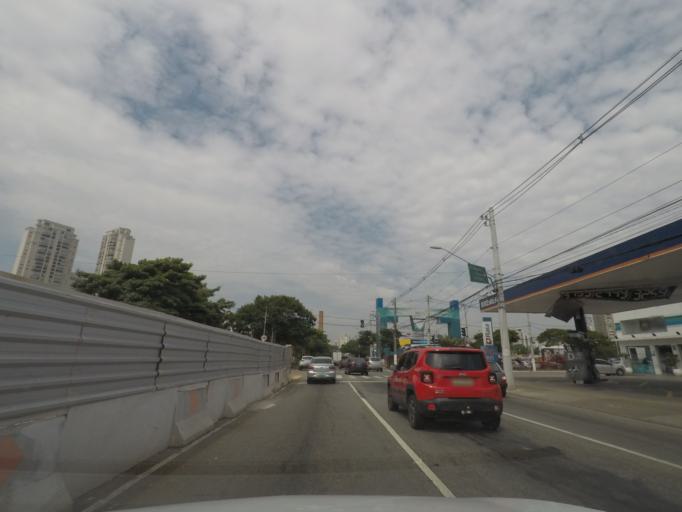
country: BR
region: Sao Paulo
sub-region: Sao Paulo
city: Sao Paulo
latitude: -23.5926
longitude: -46.6210
